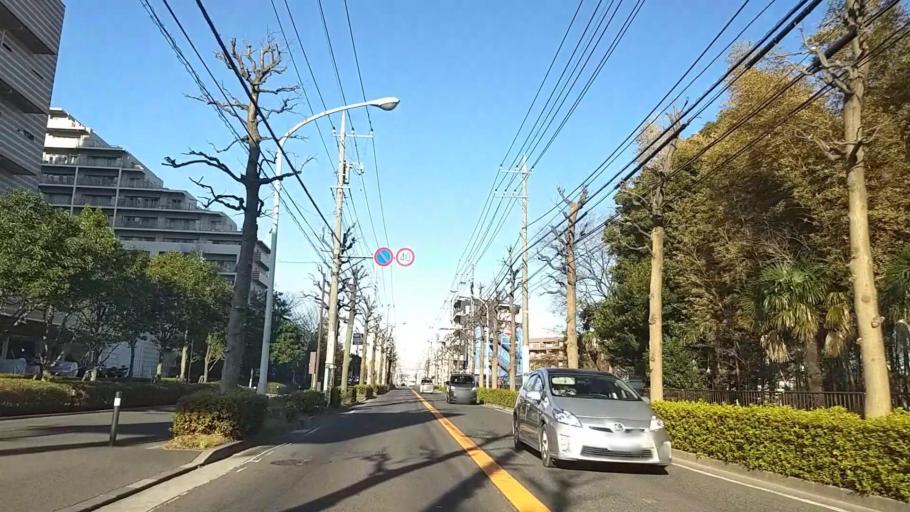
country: JP
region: Tokyo
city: Chofugaoka
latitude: 35.6090
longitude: 139.6056
